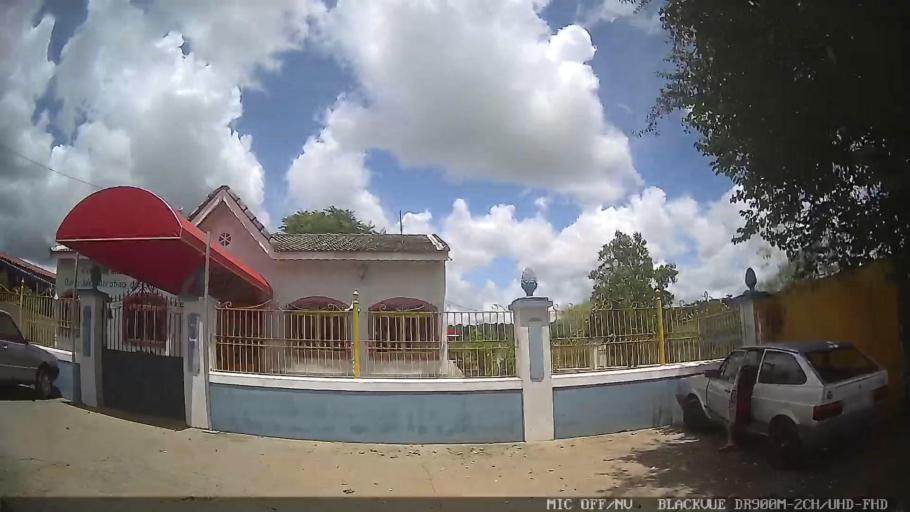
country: BR
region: Sao Paulo
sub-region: Amparo
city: Amparo
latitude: -22.8147
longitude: -46.6961
